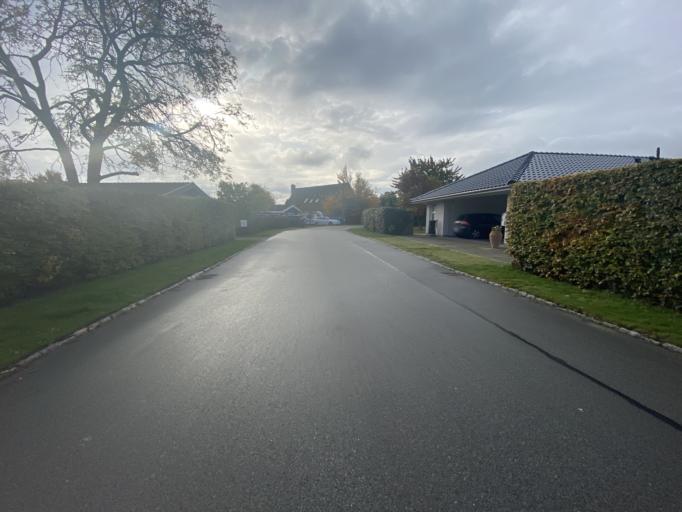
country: DK
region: Capital Region
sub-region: Dragor Kommune
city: Dragor
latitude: 55.5853
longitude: 12.6474
